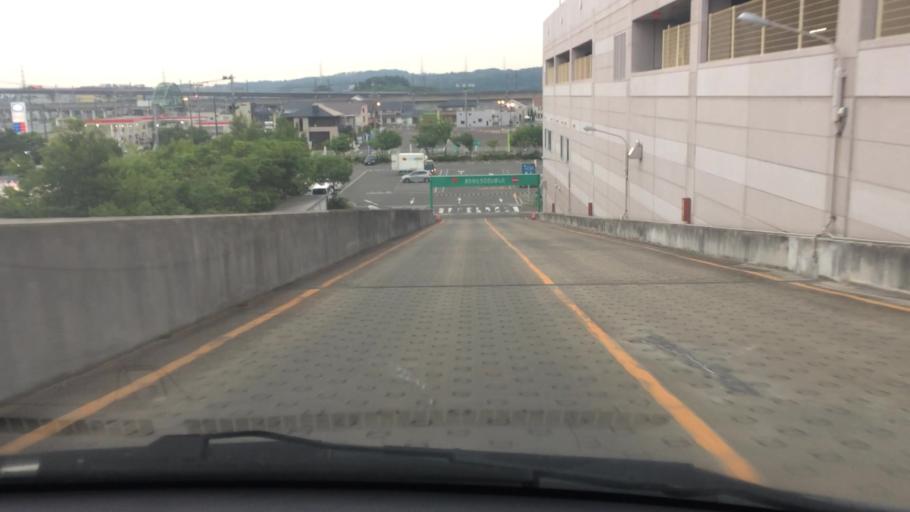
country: JP
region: Miyagi
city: Rifu
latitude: 38.3257
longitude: 140.9728
